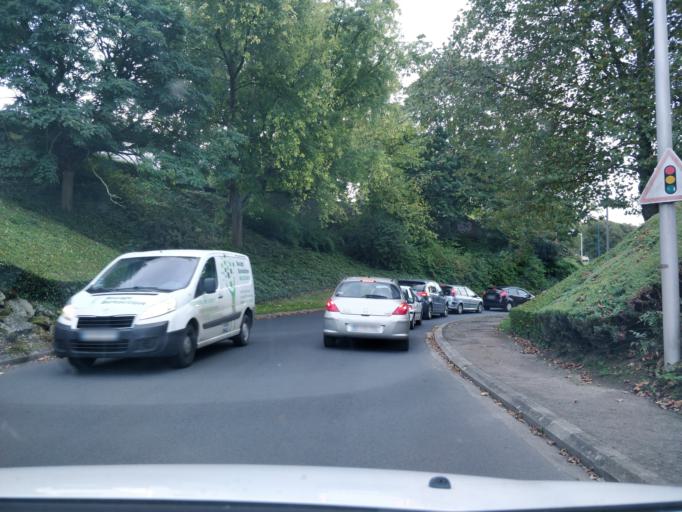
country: FR
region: Lower Normandy
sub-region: Departement du Calvados
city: Vire
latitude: 48.8456
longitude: -0.8858
